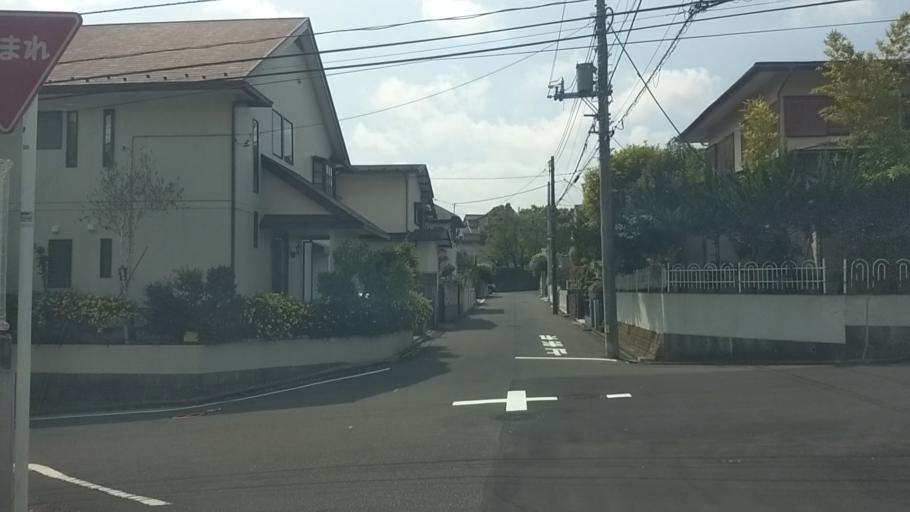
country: JP
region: Kanagawa
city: Yokohama
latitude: 35.3887
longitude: 139.5948
